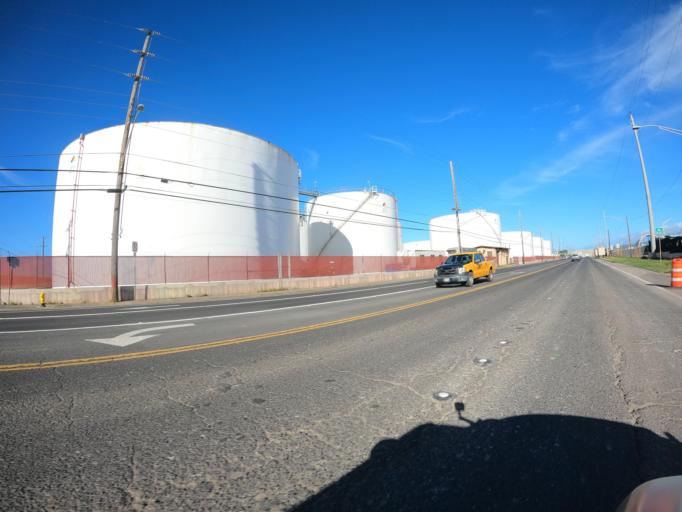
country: US
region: Hawaii
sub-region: Honolulu County
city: Honolulu
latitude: 21.3169
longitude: -157.8892
